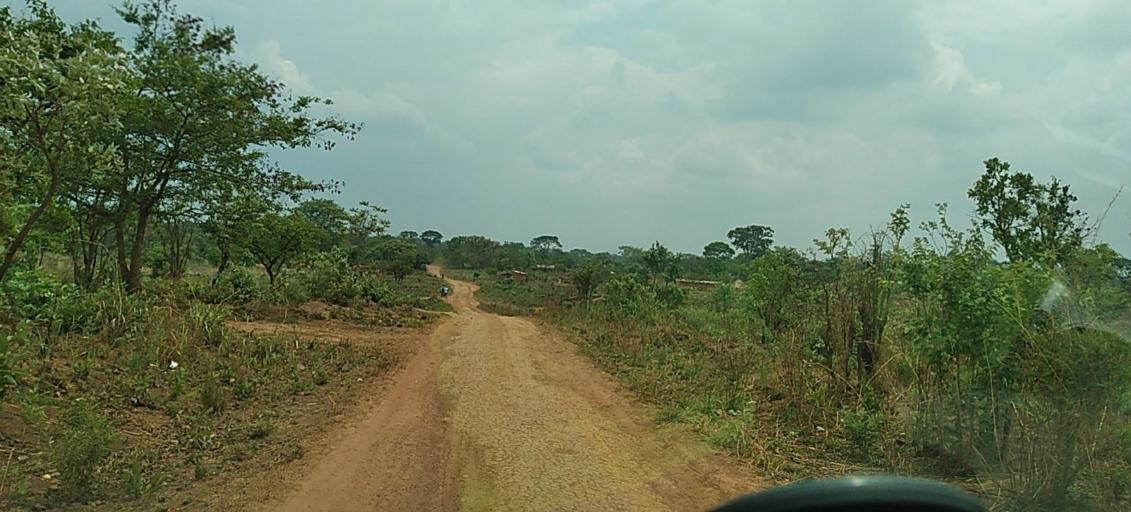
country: ZM
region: North-Western
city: Kansanshi
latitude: -11.9927
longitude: 26.2821
